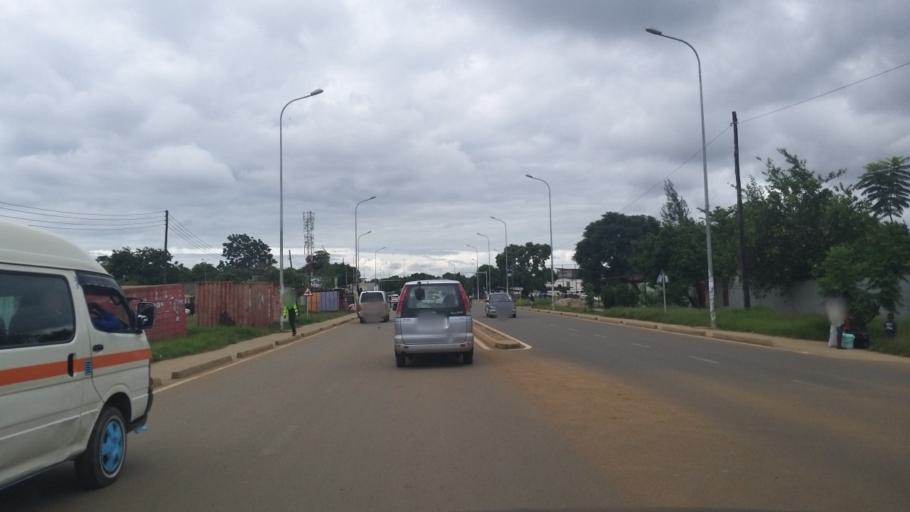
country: ZM
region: Lusaka
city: Lusaka
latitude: -15.4385
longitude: 28.3114
